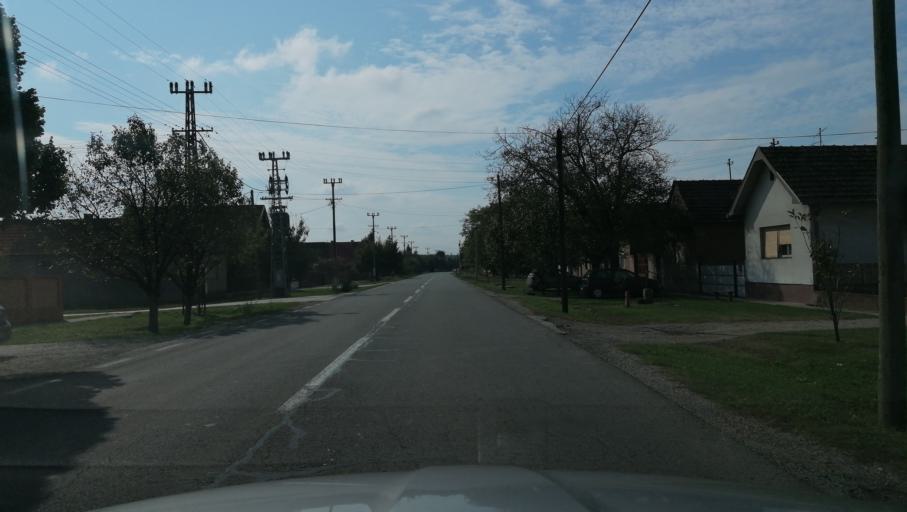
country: RS
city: Bosut
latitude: 44.9320
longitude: 19.3634
